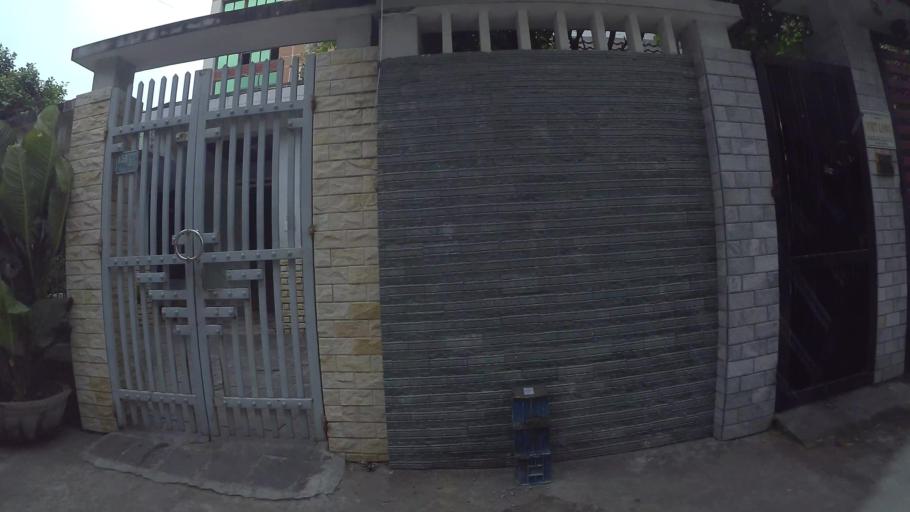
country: VN
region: Da Nang
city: Thanh Khe
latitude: 16.0720
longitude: 108.1793
